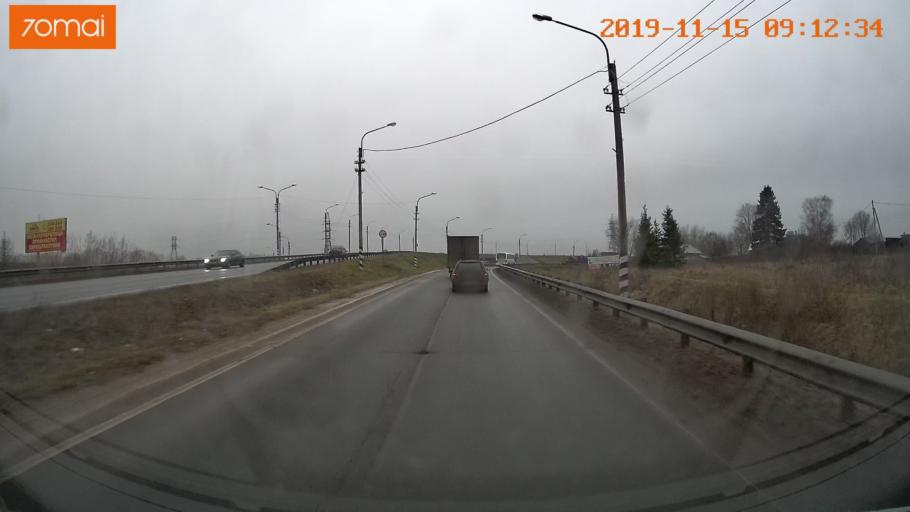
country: RU
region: Vologda
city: Tonshalovo
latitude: 59.2092
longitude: 37.9359
